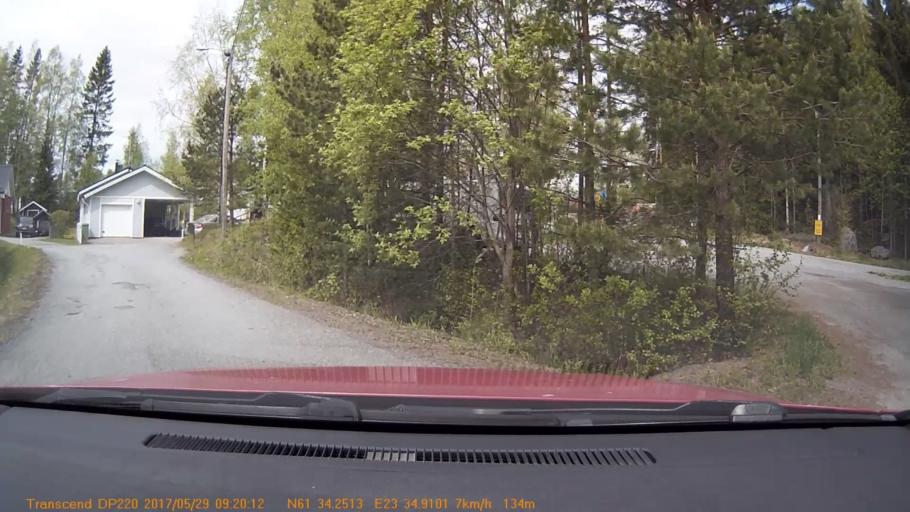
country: FI
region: Pirkanmaa
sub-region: Tampere
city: Yloejaervi
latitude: 61.5709
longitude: 23.5816
